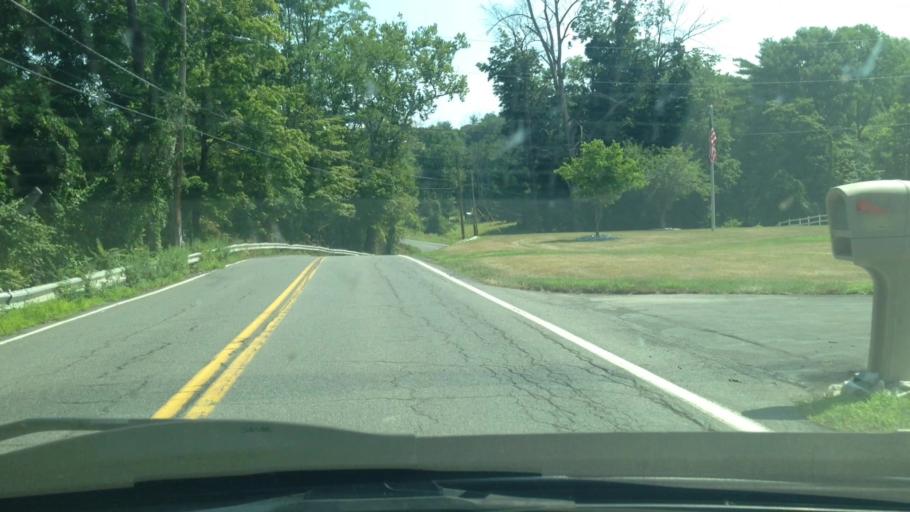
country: US
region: New York
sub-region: Ulster County
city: Kingston
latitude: 41.8990
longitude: -74.0109
